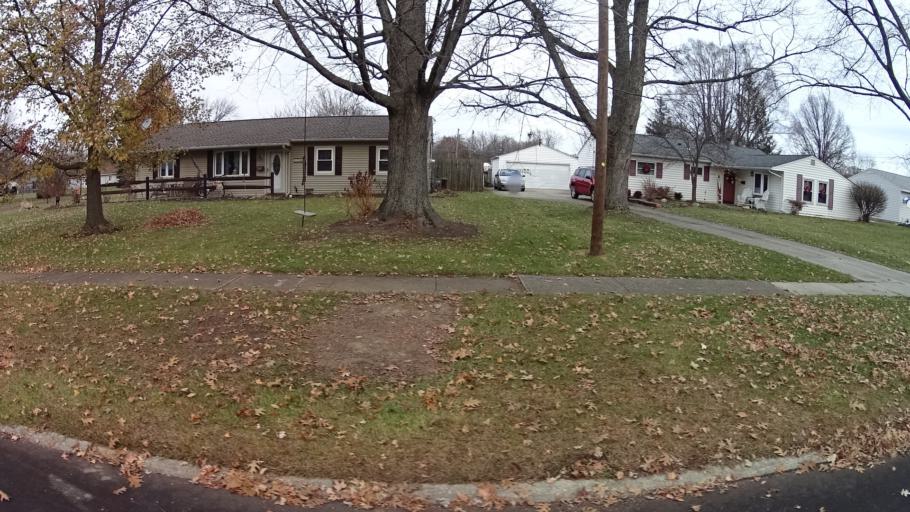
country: US
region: Ohio
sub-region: Lorain County
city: North Ridgeville
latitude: 41.3820
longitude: -81.9933
